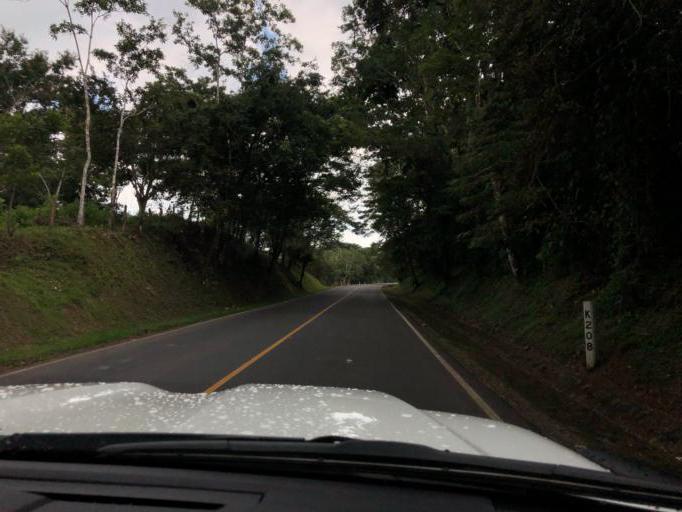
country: NI
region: Chontales
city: Villa Sandino
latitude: 11.9977
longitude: -84.8819
